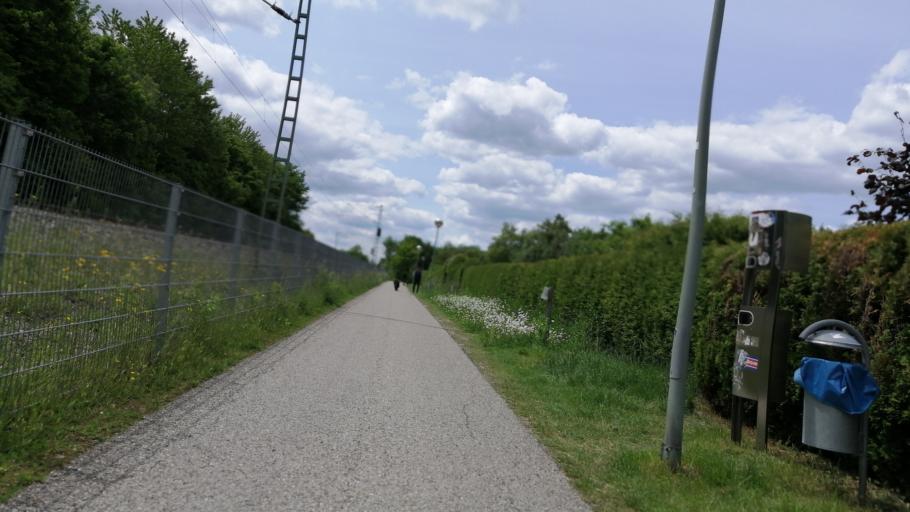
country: DE
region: Bavaria
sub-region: Upper Bavaria
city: Taufkirchen
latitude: 48.0440
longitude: 11.6027
